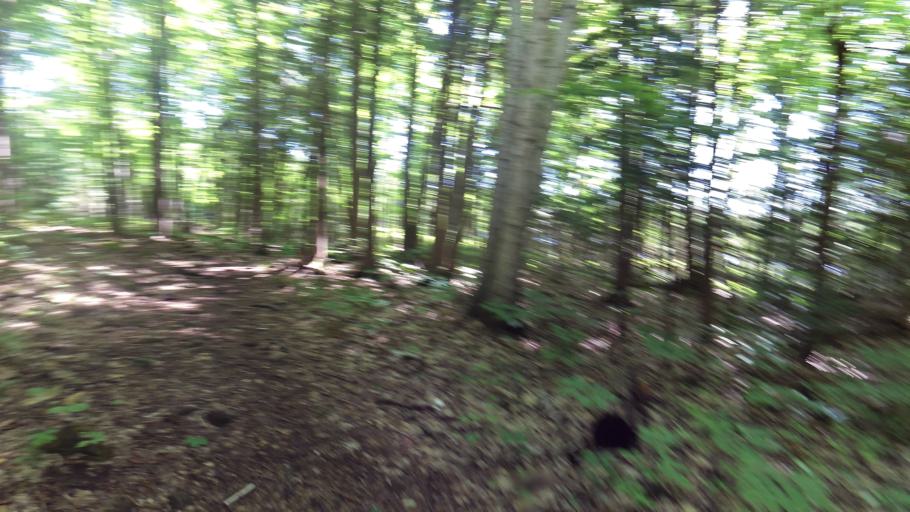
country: CA
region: Ontario
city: Arnprior
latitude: 45.4625
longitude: -76.2613
